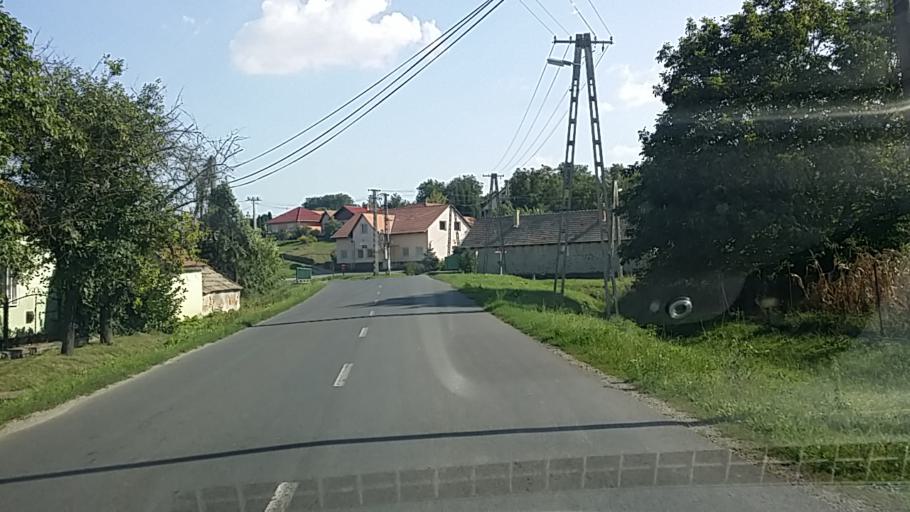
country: HU
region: Nograd
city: Bujak
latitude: 47.8819
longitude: 19.5501
